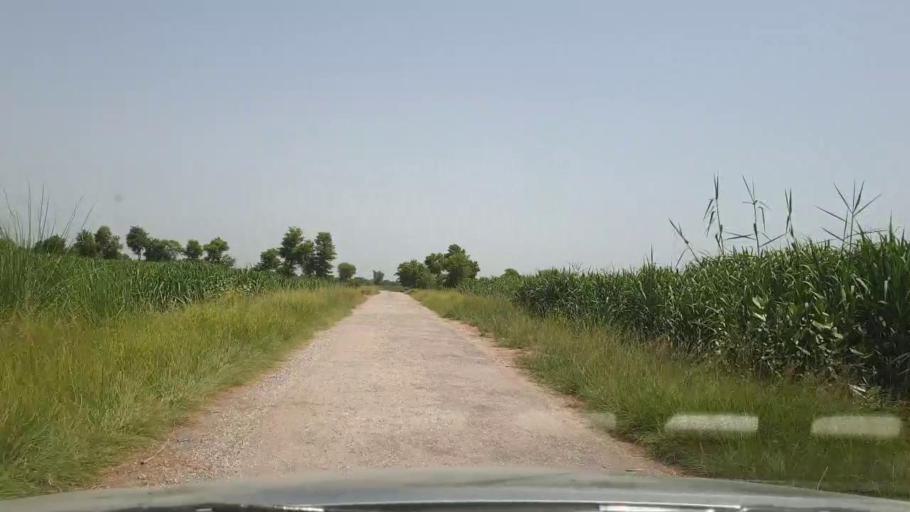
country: PK
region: Sindh
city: Pano Aqil
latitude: 27.8069
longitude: 69.2384
